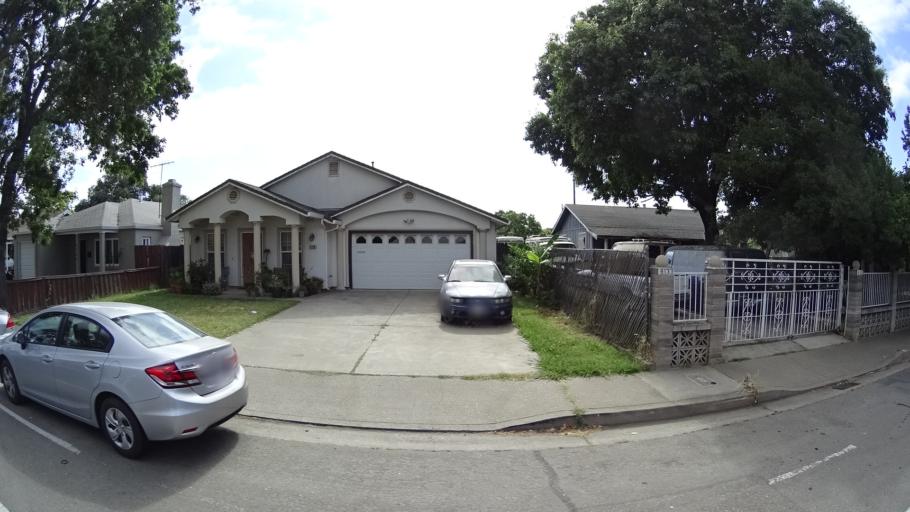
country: US
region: California
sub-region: Sacramento County
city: Parkway
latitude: 38.5141
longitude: -121.4831
